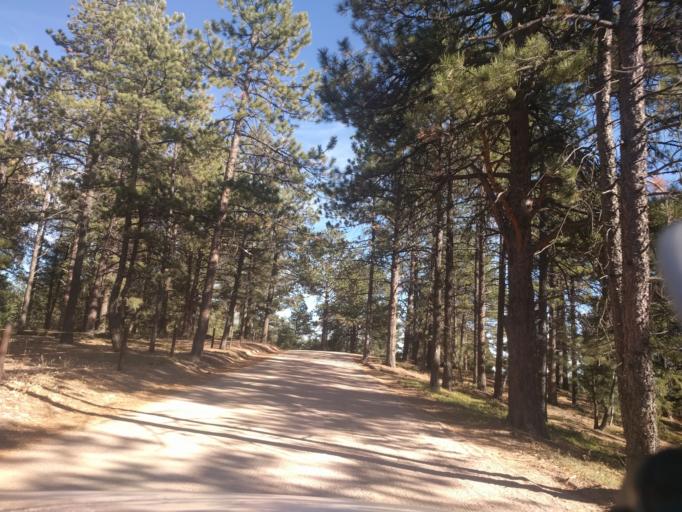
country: US
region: Colorado
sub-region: Douglas County
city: Perry Park
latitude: 39.3035
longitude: -105.0868
